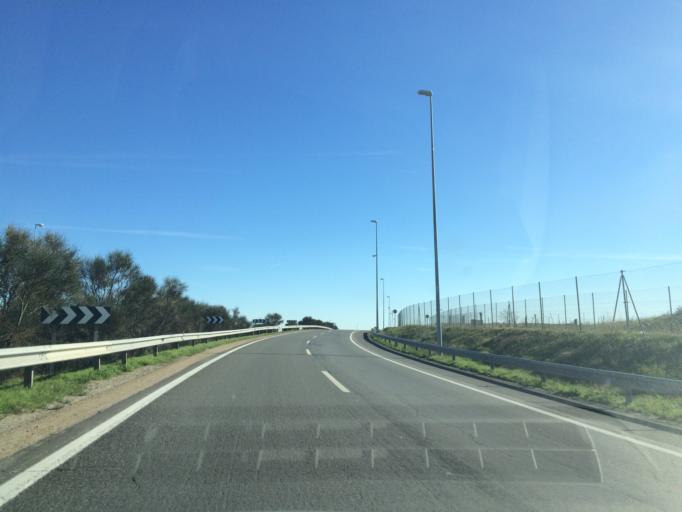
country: ES
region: Madrid
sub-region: Provincia de Madrid
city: Colmenar Viejo
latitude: 40.6522
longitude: -3.7379
